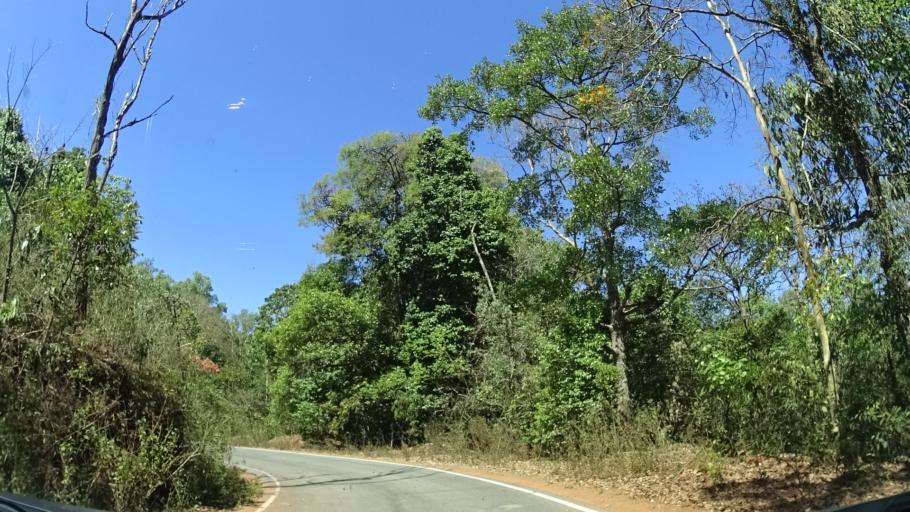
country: IN
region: Karnataka
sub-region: Chikmagalur
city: Sringeri
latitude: 13.2120
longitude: 75.2703
